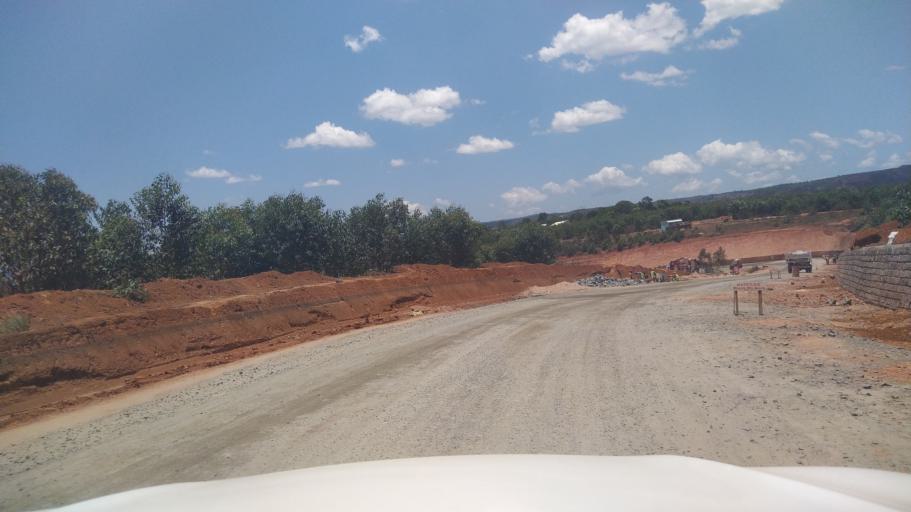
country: MG
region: Analamanga
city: Anjozorobe
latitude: -18.5184
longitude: 48.2627
